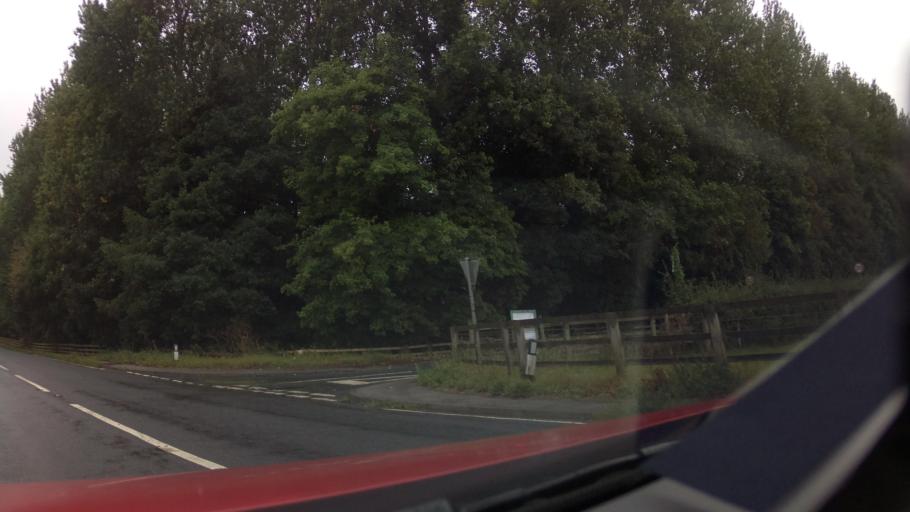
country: GB
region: England
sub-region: North Yorkshire
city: Pannal
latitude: 53.9181
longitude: -1.5289
